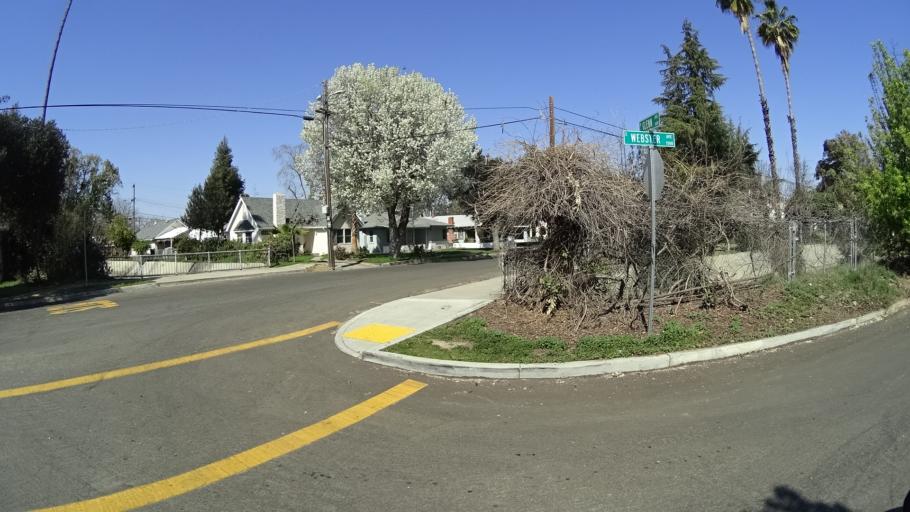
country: US
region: California
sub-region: Fresno County
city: Fresno
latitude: 36.7566
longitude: -119.7928
